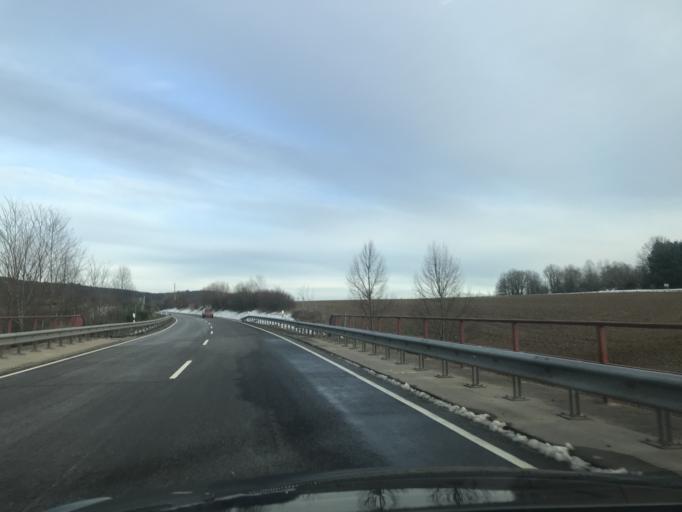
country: DE
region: Rheinland-Pfalz
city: Hochspeyer
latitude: 49.4495
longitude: 7.8965
